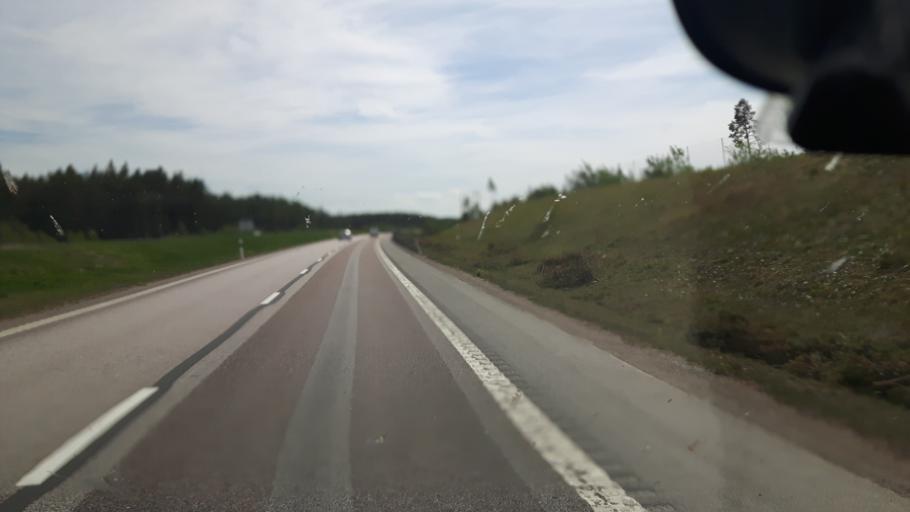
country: SE
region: Uppsala
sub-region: Tierps Kommun
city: Tierp
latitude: 60.3138
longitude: 17.5204
